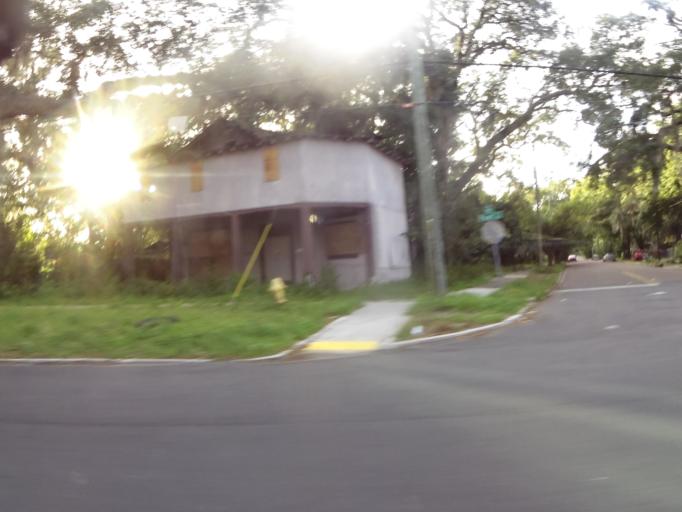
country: US
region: Florida
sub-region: Duval County
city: Jacksonville
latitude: 30.3666
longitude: -81.6566
